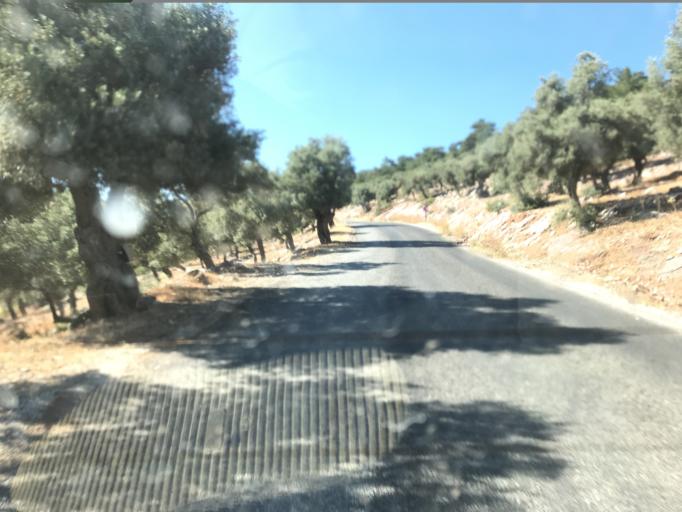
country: TR
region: Mugla
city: Selimiye
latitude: 37.3842
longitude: 27.4843
